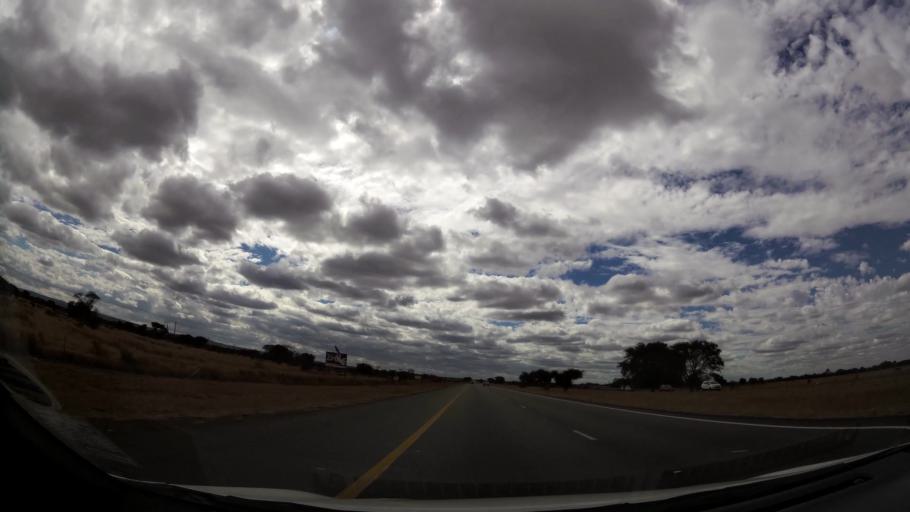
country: ZA
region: Limpopo
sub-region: Waterberg District Municipality
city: Bela-Bela
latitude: -24.9408
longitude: 28.3649
